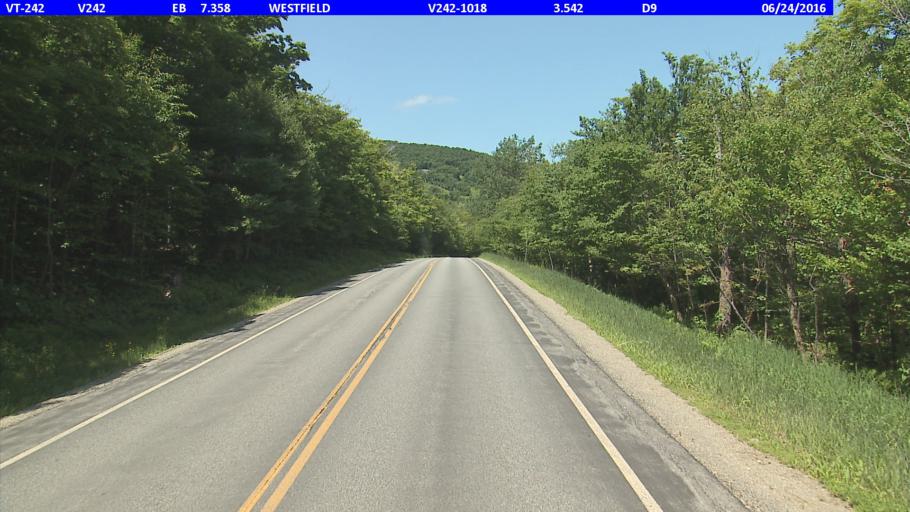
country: US
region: Vermont
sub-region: Franklin County
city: Richford
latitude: 44.9253
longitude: -72.4990
